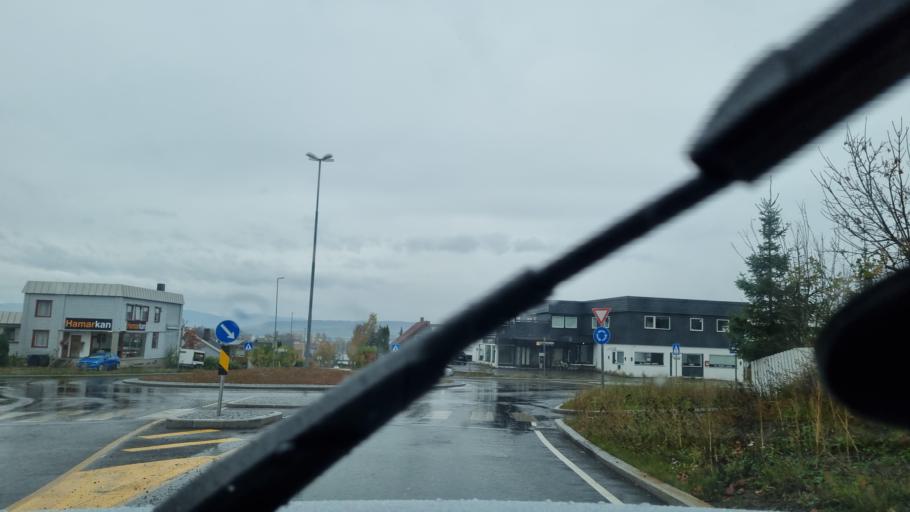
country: NO
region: Hedmark
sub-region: Hamar
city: Hamar
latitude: 60.8032
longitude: 11.0478
